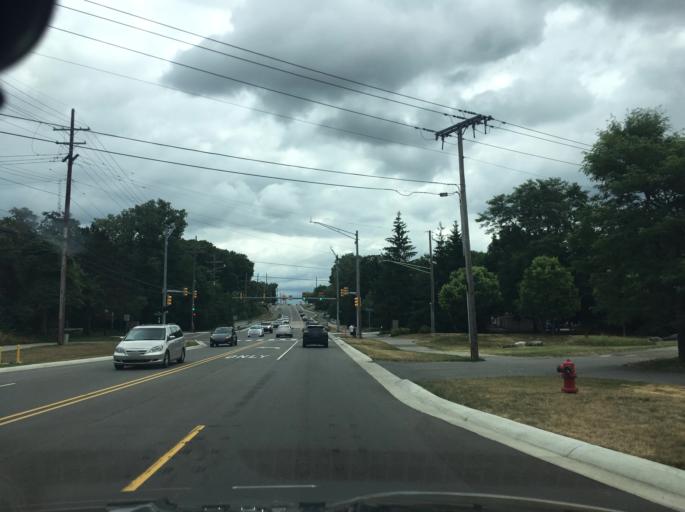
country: US
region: Michigan
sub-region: Oakland County
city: Rochester
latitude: 42.6953
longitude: -83.1484
